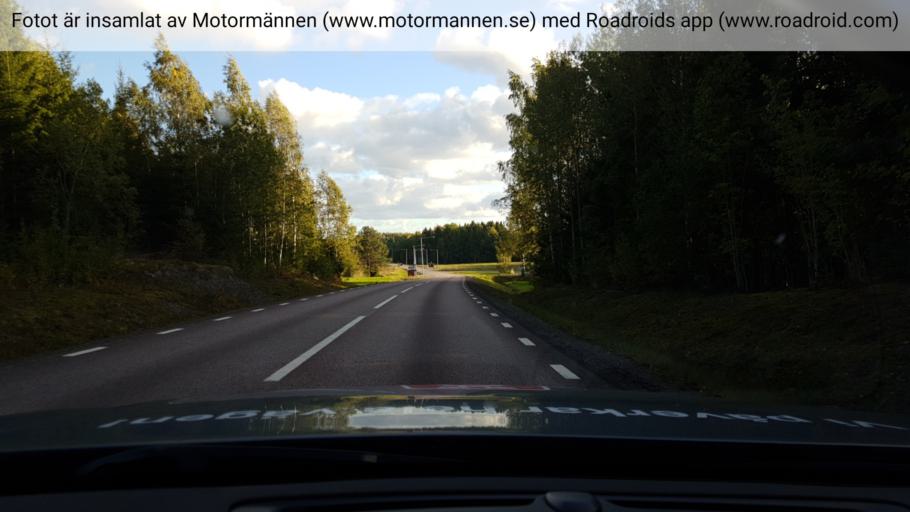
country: SE
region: Vaermland
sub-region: Karlstads Kommun
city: Molkom
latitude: 59.6433
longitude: 13.7157
